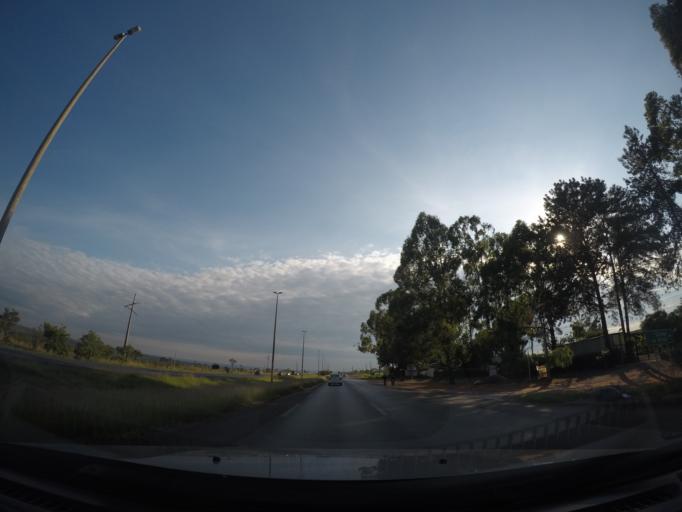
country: BR
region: Goias
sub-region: Planaltina
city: Planaltina
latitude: -15.6381
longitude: -47.7476
